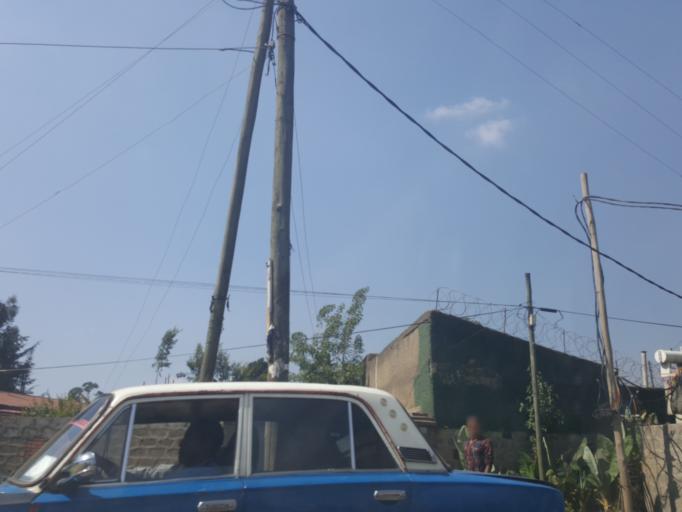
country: ET
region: Adis Abeba
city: Addis Ababa
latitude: 9.0515
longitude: 38.7332
